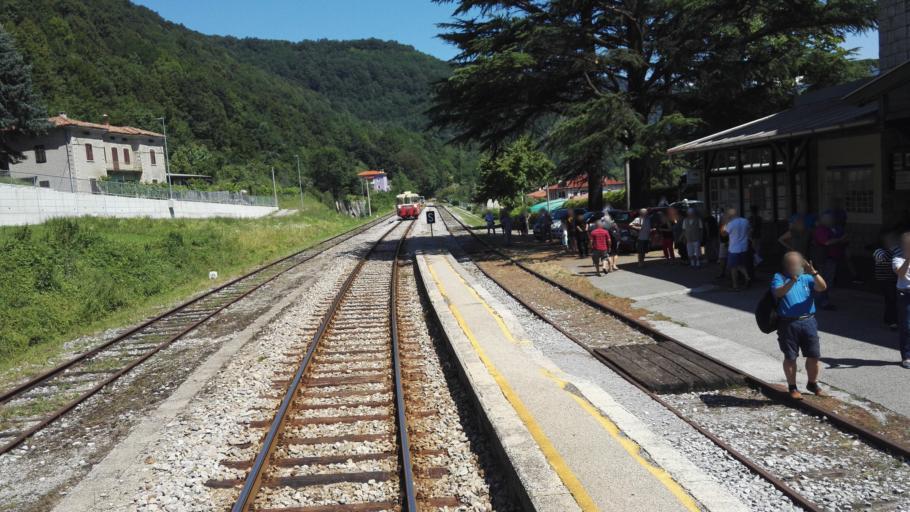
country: SI
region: Kanal
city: Kanal
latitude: 46.0838
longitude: 13.6317
